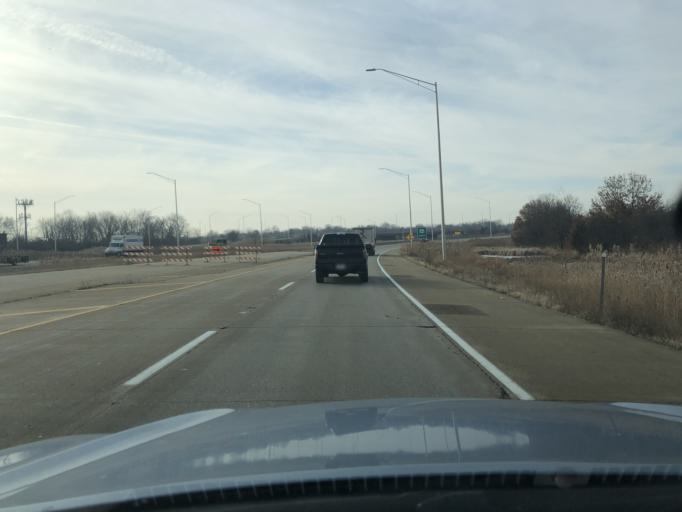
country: US
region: Illinois
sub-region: DuPage County
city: Hanover Park
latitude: 41.9840
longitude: -88.1343
